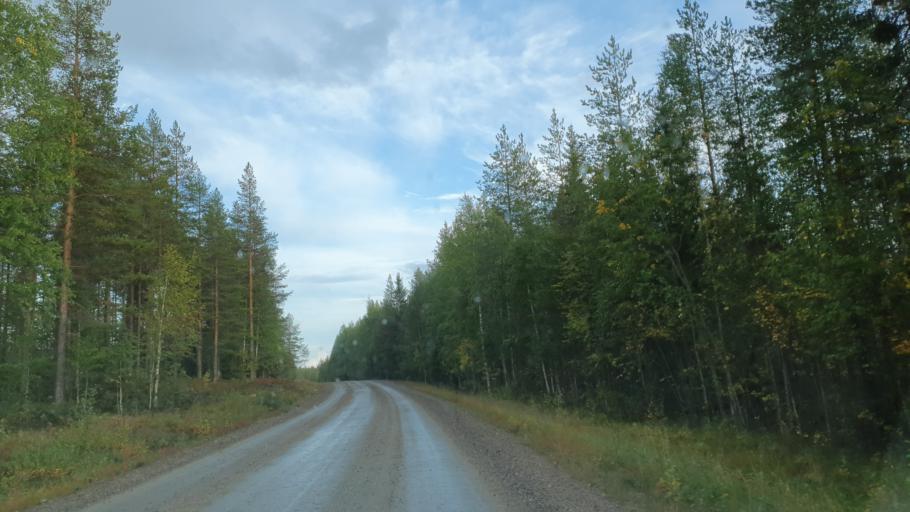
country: FI
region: Kainuu
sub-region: Kehys-Kainuu
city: Kuhmo
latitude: 64.4159
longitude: 29.5078
